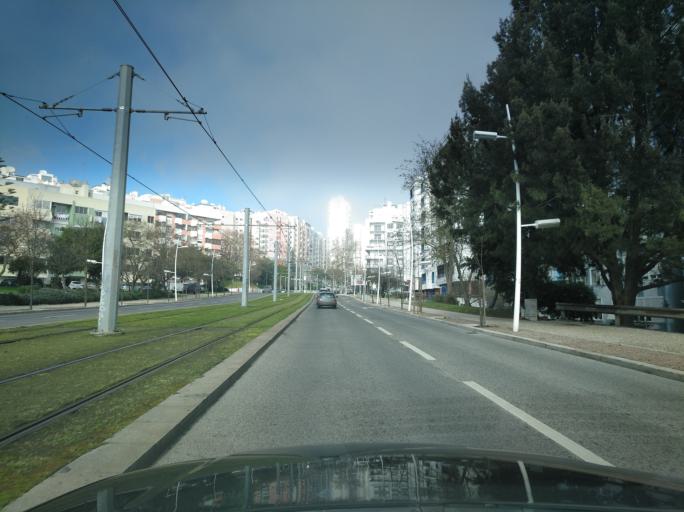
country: PT
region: Setubal
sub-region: Almada
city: Pragal
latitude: 38.6709
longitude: -9.1661
